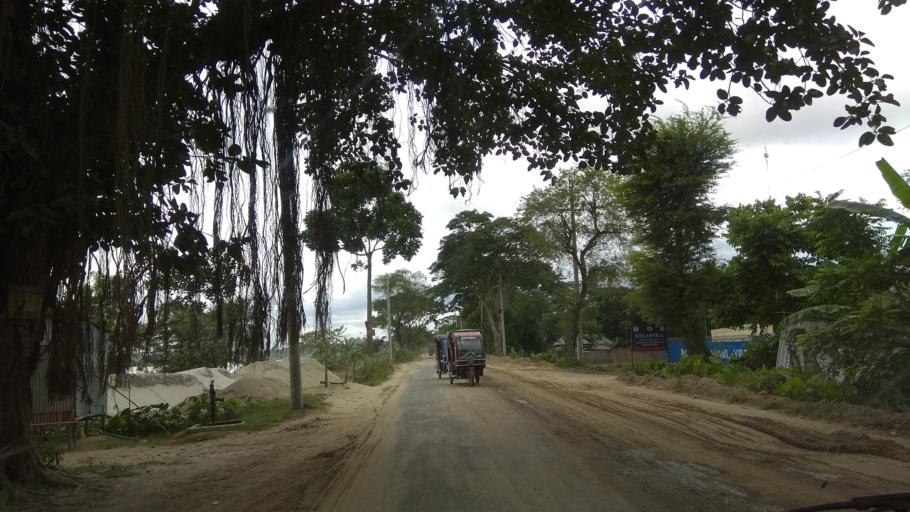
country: BD
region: Khulna
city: Kalia
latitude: 23.2014
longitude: 89.6976
